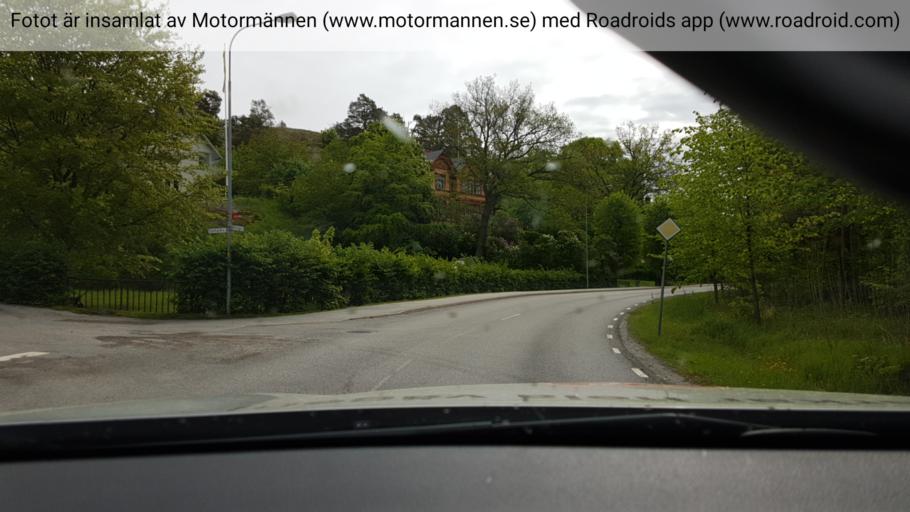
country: SE
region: Stockholm
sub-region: Nacka Kommun
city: Saltsjobaden
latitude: 59.2825
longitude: 18.3050
